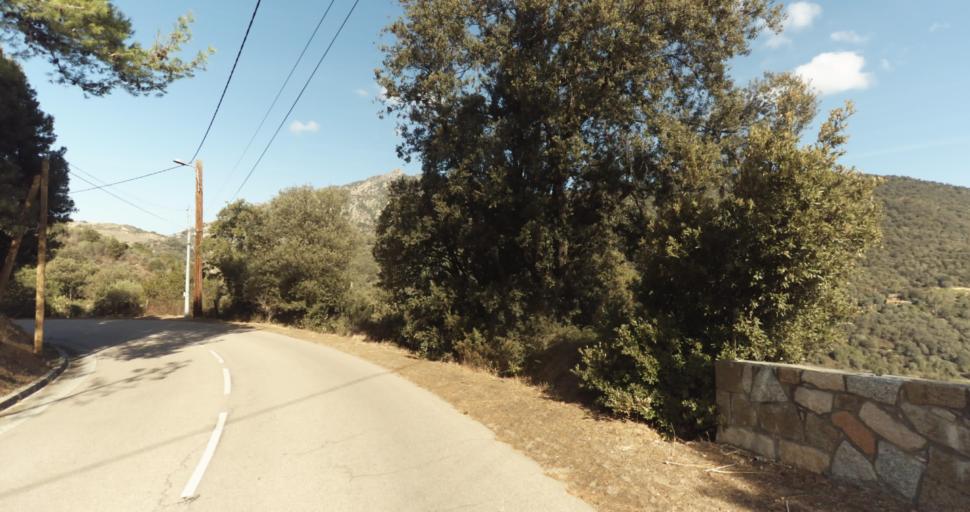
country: FR
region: Corsica
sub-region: Departement de la Corse-du-Sud
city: Ajaccio
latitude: 41.9270
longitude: 8.7081
